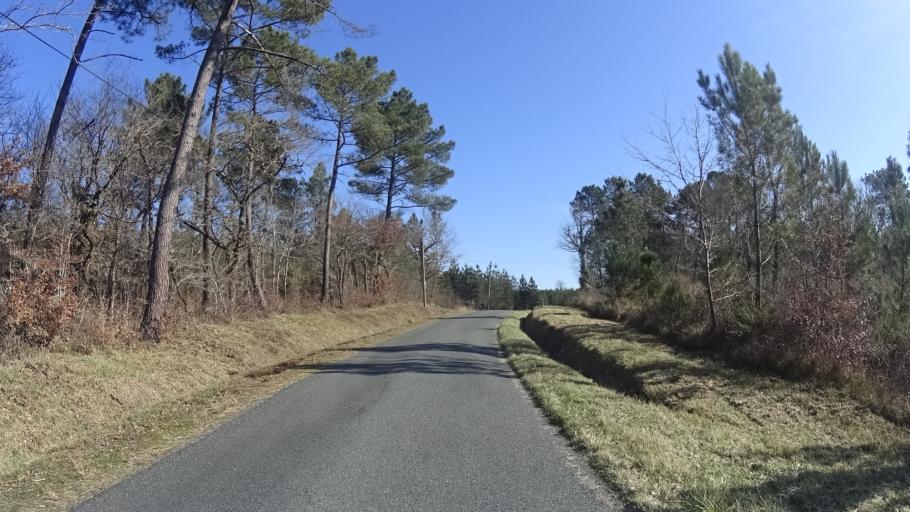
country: FR
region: Aquitaine
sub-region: Departement de la Dordogne
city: Saint-Aulaye
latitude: 45.1214
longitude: 0.2086
